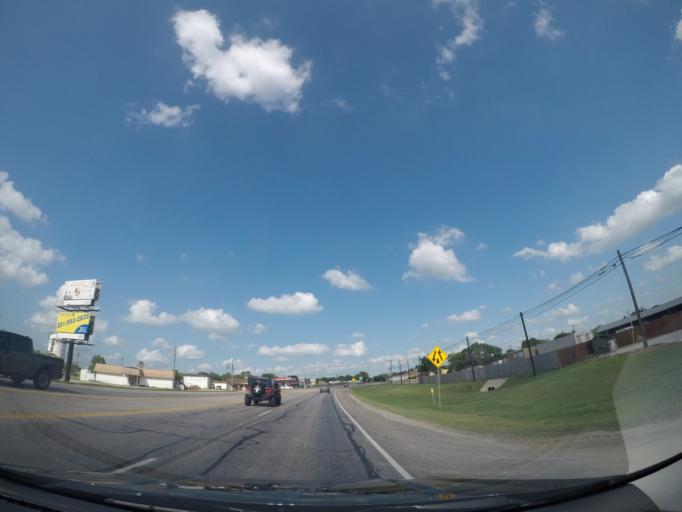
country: US
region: Texas
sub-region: Gonzales County
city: Gonzales
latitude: 29.5117
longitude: -97.4178
